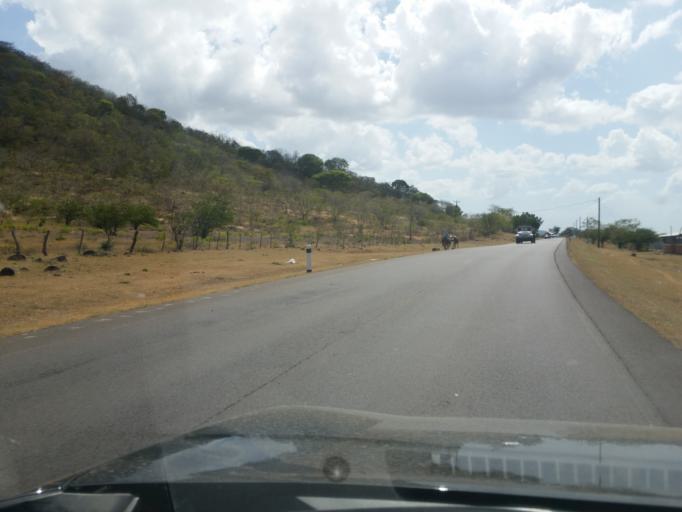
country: NI
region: Boaco
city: San Lorenzo
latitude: 12.2399
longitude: -85.6459
